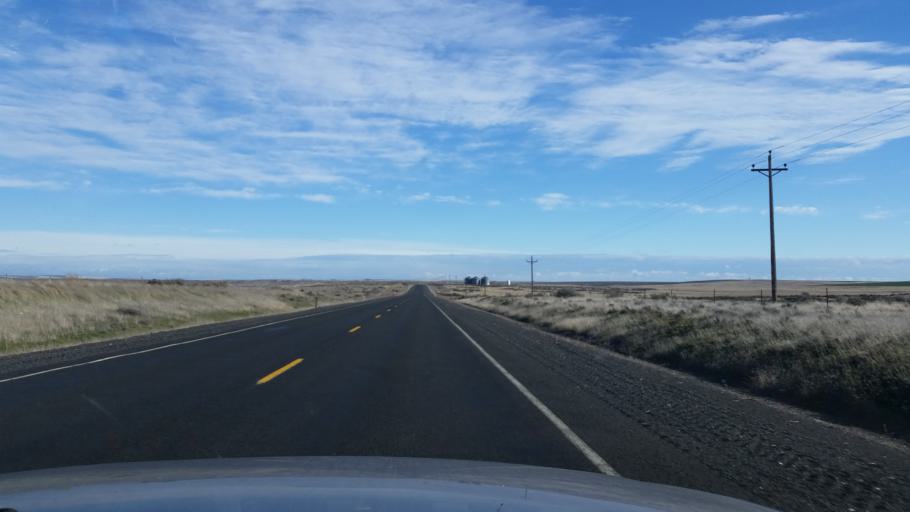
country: US
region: Washington
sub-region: Grant County
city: Warden
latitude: 47.3143
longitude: -118.7902
